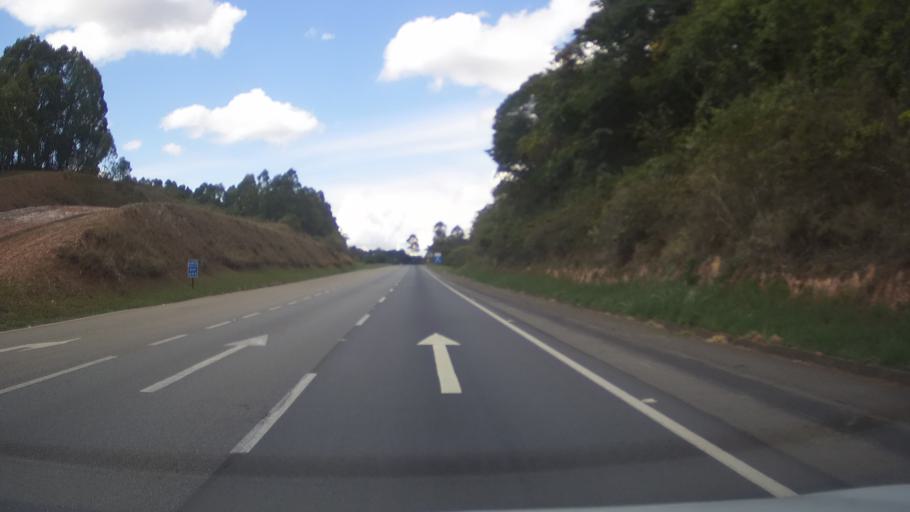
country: BR
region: Minas Gerais
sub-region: Santo Antonio Do Amparo
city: Santo Antonio do Amparo
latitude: -20.8521
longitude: -44.8355
